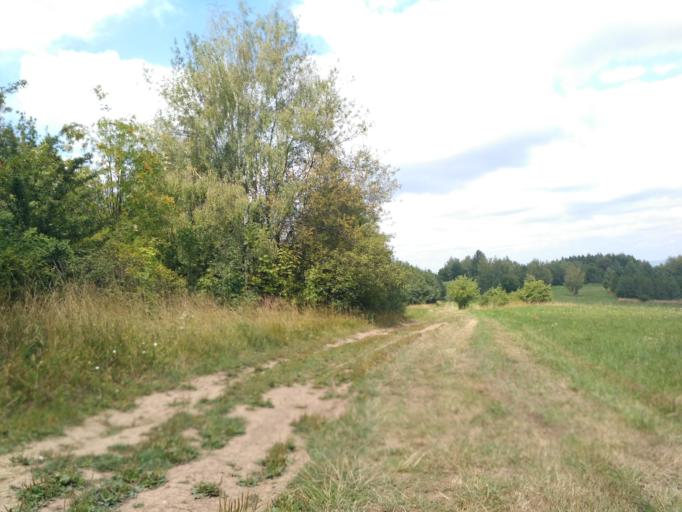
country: PL
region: Subcarpathian Voivodeship
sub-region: Powiat krosnienski
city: Iwonicz-Zdroj
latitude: 49.5737
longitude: 21.8089
